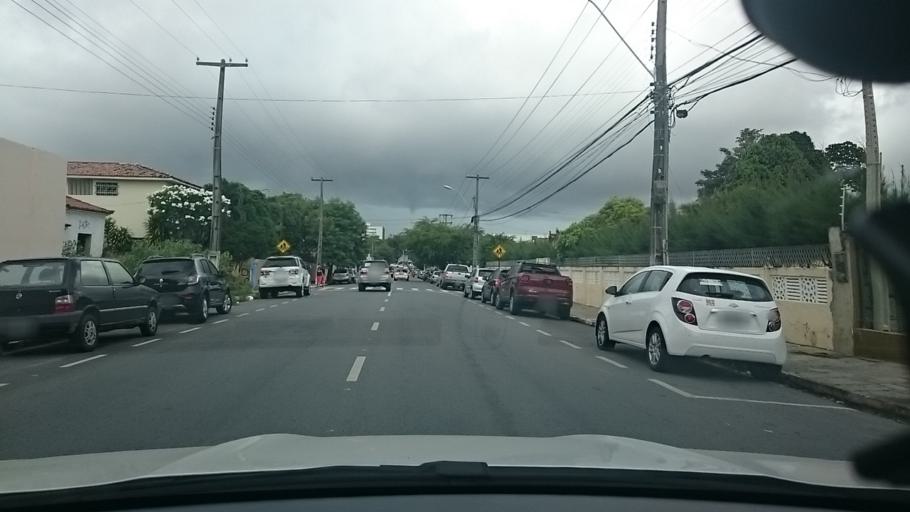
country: BR
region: Paraiba
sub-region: Joao Pessoa
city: Joao Pessoa
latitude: -7.1212
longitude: -34.8696
